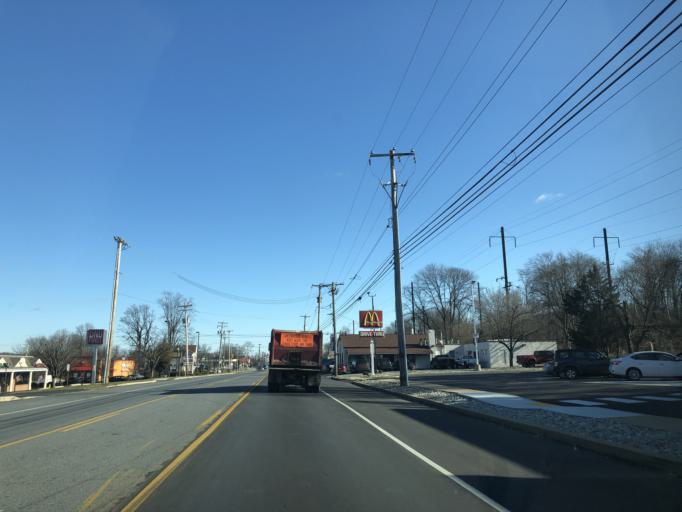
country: US
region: Pennsylvania
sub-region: Chester County
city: Caln
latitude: 39.9887
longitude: -75.7899
